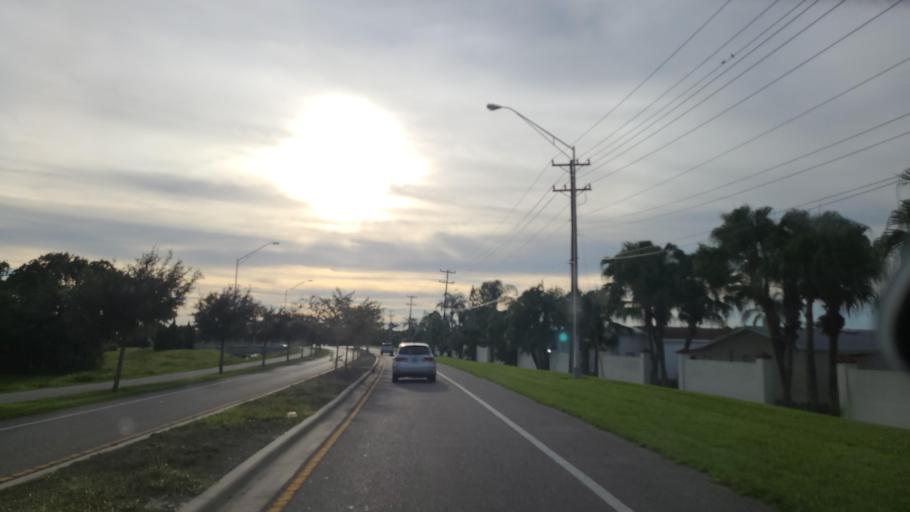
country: US
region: Florida
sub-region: Polk County
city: Lakeland
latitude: 28.0104
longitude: -81.9721
